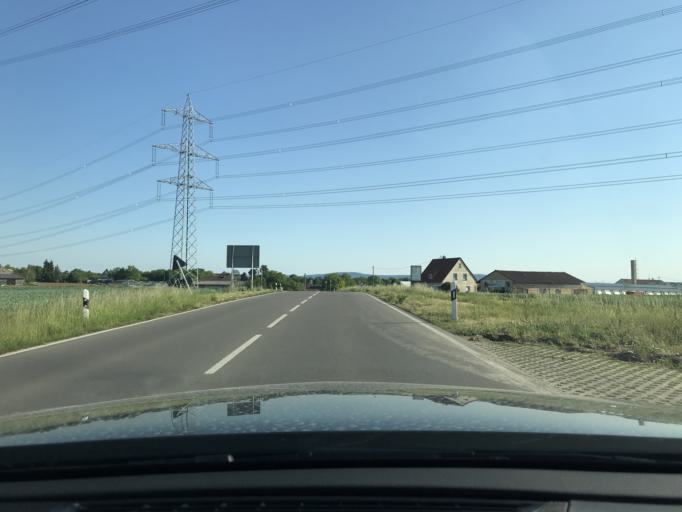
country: DE
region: Baden-Wuerttemberg
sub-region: Regierungsbezirk Stuttgart
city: Schwaikheim
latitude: 48.8722
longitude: 9.3187
